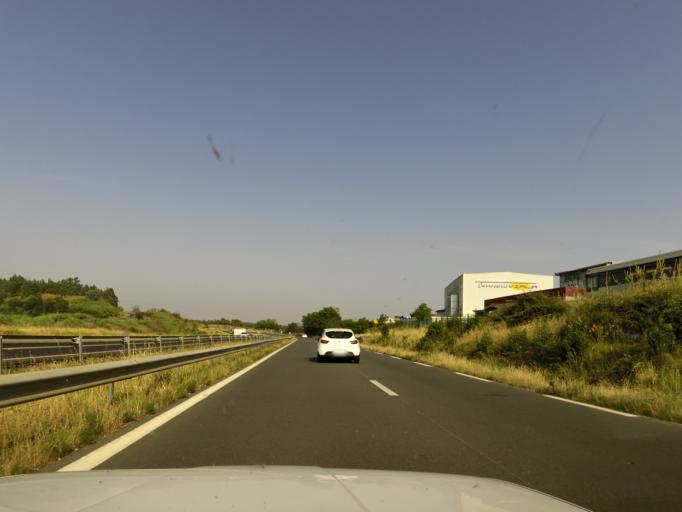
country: FR
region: Languedoc-Roussillon
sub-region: Departement de l'Herault
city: Grabels
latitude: 43.6295
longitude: 3.7715
